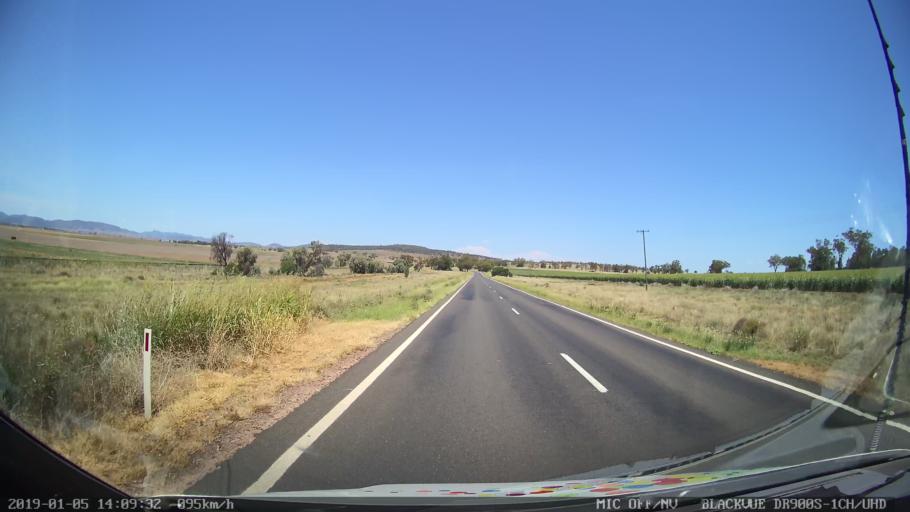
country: AU
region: New South Wales
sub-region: Gunnedah
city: Gunnedah
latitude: -31.2433
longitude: 150.4285
